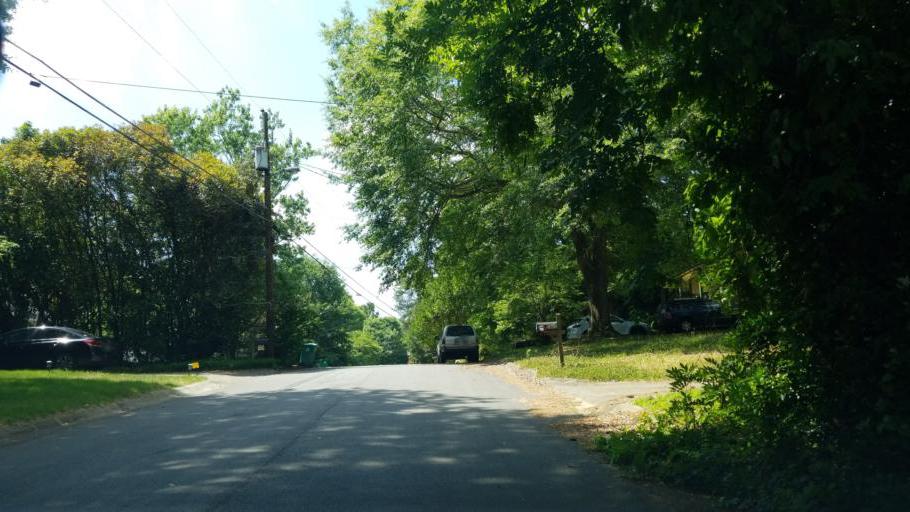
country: US
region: Georgia
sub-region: Cobb County
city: Smyrna
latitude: 33.8882
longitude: -84.4851
